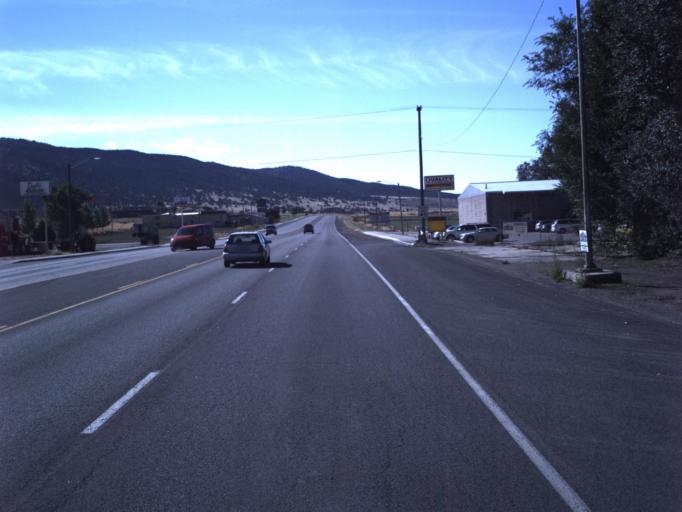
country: US
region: Utah
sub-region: Juab County
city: Nephi
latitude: 39.6971
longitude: -111.8362
